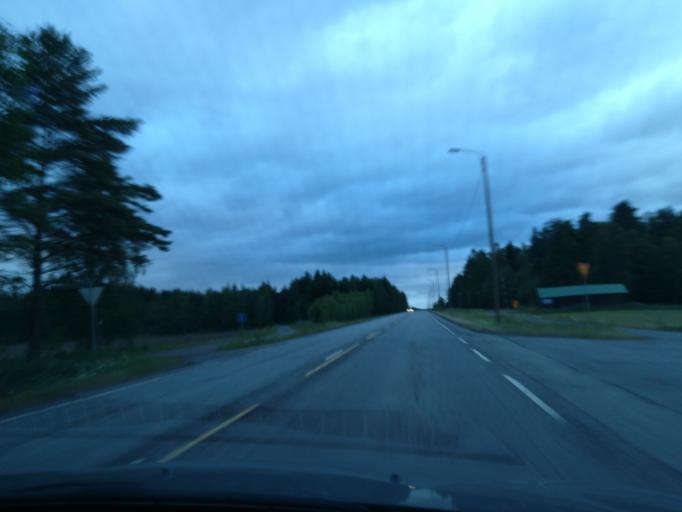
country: FI
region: Southern Savonia
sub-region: Mikkeli
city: Ristiina
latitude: 61.4782
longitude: 27.2531
